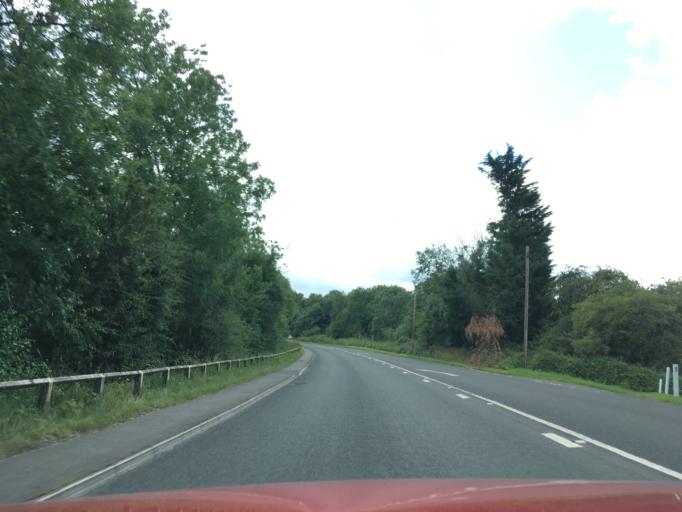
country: GB
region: England
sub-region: Nottinghamshire
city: Ruddington
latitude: 52.8499
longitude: -1.1398
